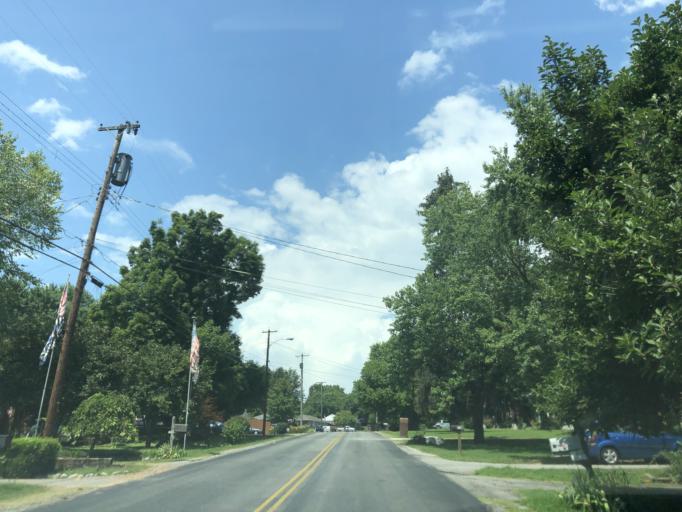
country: US
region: Tennessee
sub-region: Davidson County
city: Lakewood
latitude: 36.1536
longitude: -86.6560
